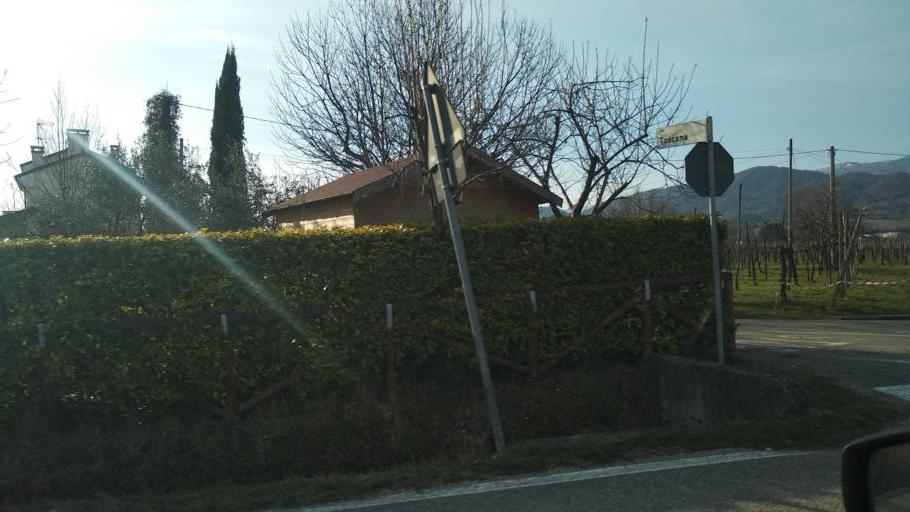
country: IT
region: Veneto
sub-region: Provincia di Treviso
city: Vittorio Veneto
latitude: 45.9605
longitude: 12.3072
